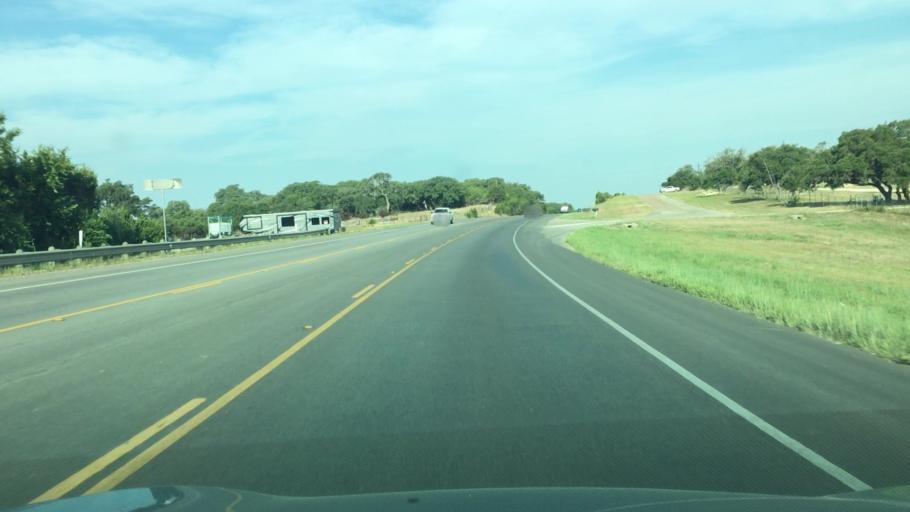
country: US
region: Texas
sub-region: Hays County
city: Dripping Springs
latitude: 30.1978
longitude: -98.1638
